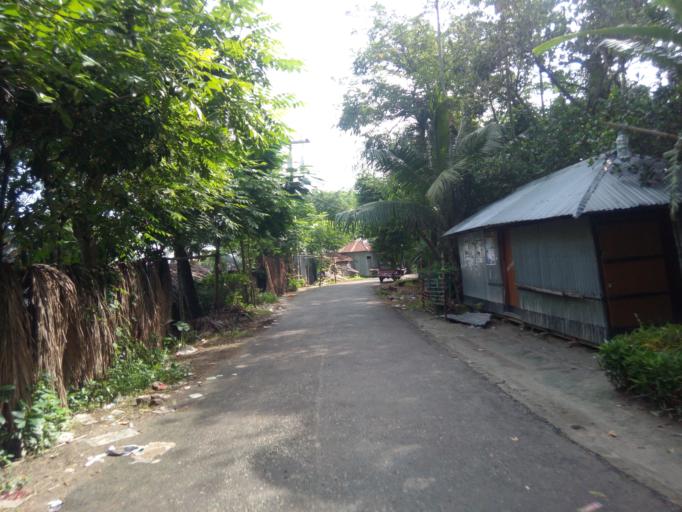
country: BD
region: Khulna
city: Kalia
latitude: 22.9600
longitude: 89.5554
